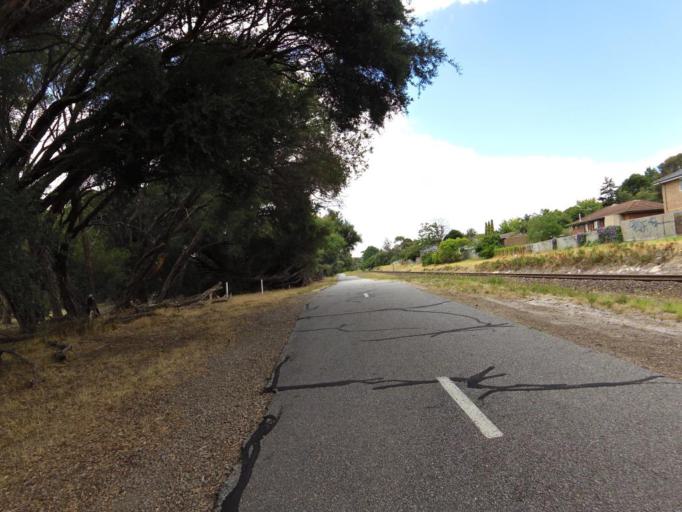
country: AU
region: Victoria
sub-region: Frankston
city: Frankston South
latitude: -38.1547
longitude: 145.1465
